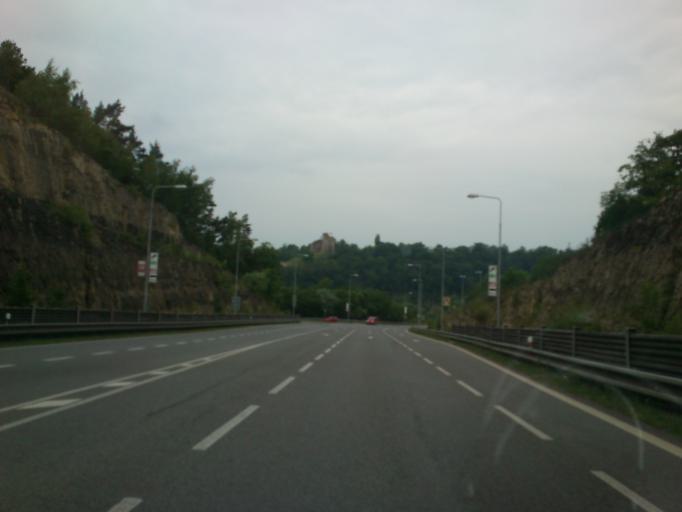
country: CZ
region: Central Bohemia
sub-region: Okres Mlada Boleslav
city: Mlada Boleslav
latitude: 50.4370
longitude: 14.8968
